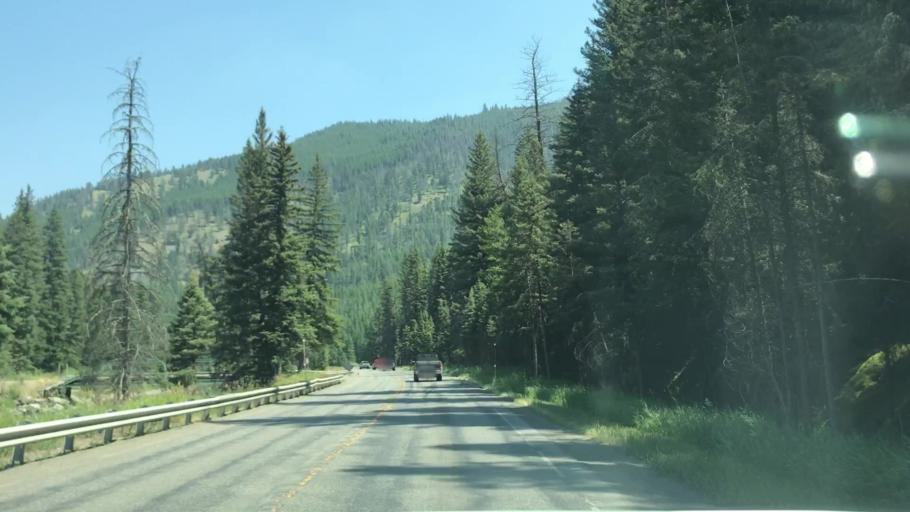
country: US
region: Montana
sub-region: Gallatin County
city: Big Sky
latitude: 45.2979
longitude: -111.2046
